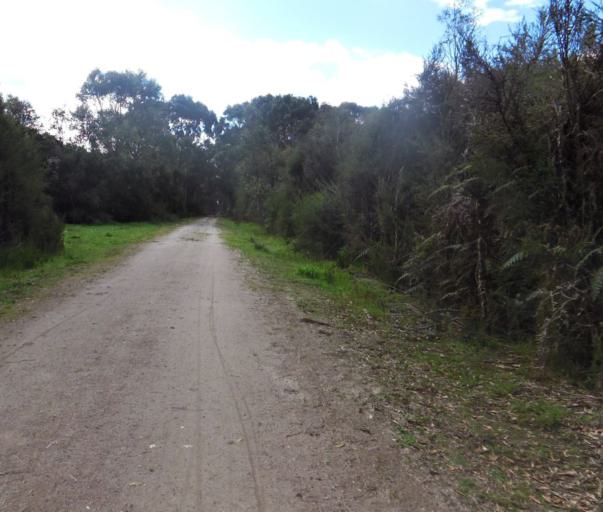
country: AU
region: Victoria
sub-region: Bass Coast
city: North Wonthaggi
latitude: -38.6249
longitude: 146.0389
